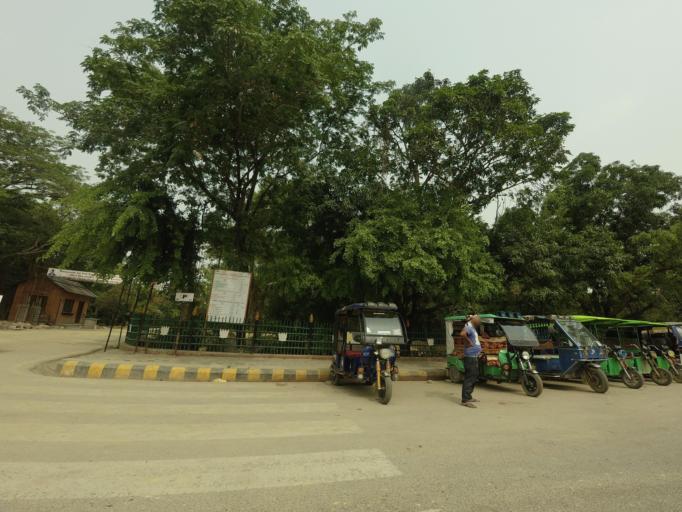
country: IN
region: Uttar Pradesh
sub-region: Maharajganj
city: Nautanwa
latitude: 27.4697
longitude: 83.2838
